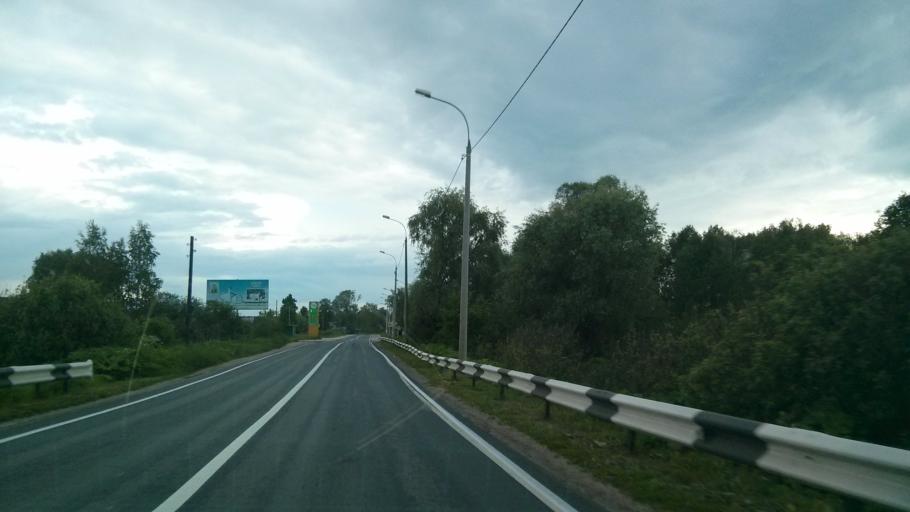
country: RU
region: Nizjnij Novgorod
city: Vacha
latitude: 55.7559
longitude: 42.5195
